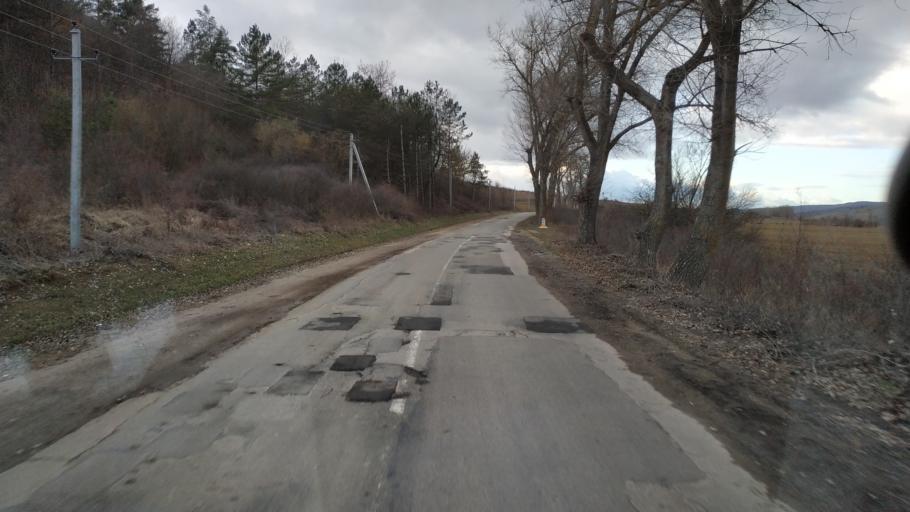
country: MD
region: Calarasi
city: Calarasi
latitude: 47.3142
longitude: 28.3345
